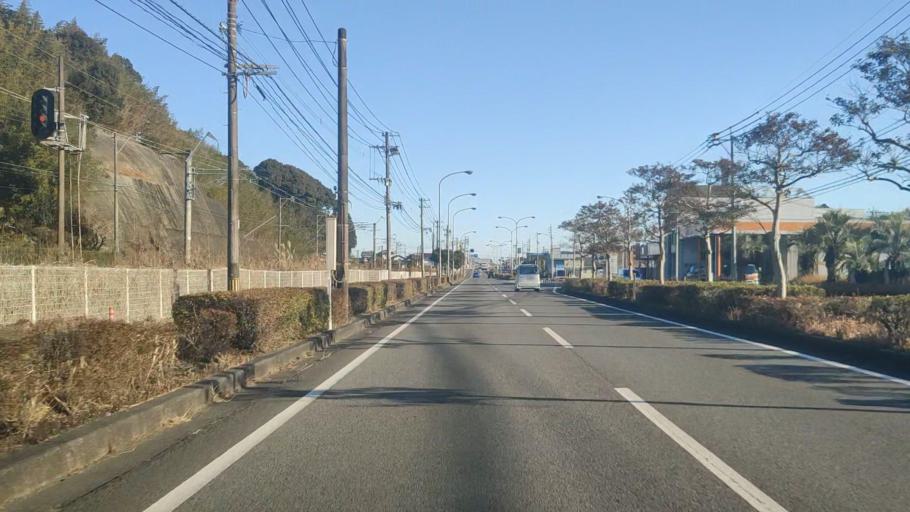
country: JP
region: Miyazaki
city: Nobeoka
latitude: 32.4546
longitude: 131.6430
